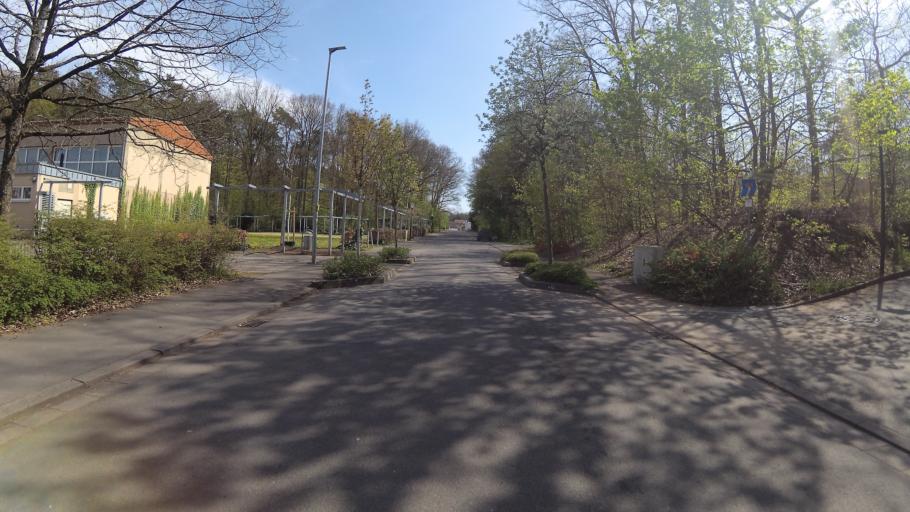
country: DE
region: Saarland
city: Homburg
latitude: 49.3441
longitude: 7.3657
